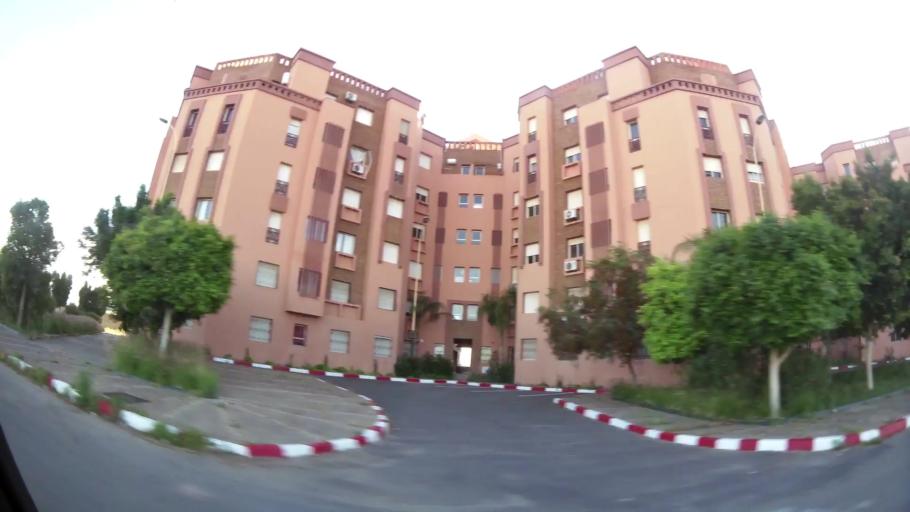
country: MA
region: Marrakech-Tensift-Al Haouz
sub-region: Marrakech
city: Marrakesh
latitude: 31.7469
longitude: -8.1283
